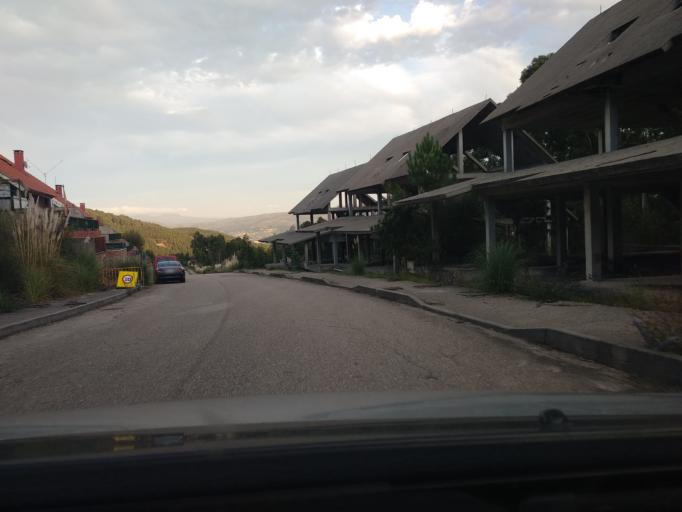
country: ES
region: Galicia
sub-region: Provincia de Pontevedra
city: Moana
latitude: 42.2971
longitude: -8.6901
